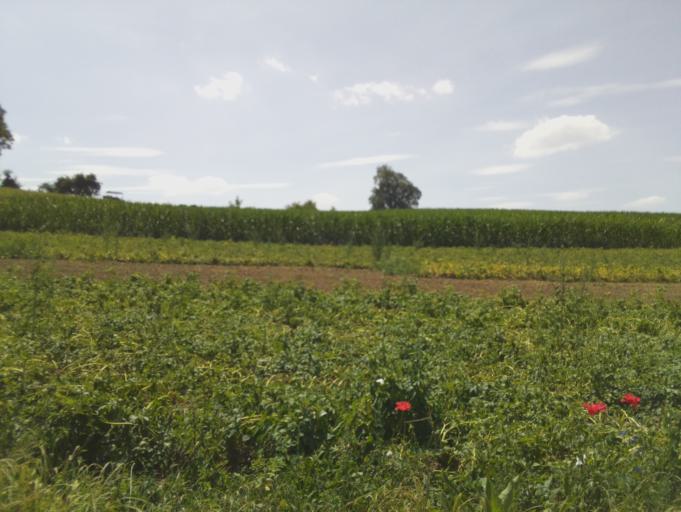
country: CH
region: Zurich
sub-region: Bezirk Andelfingen
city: Kleinandelfingen
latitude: 47.6179
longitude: 8.7197
